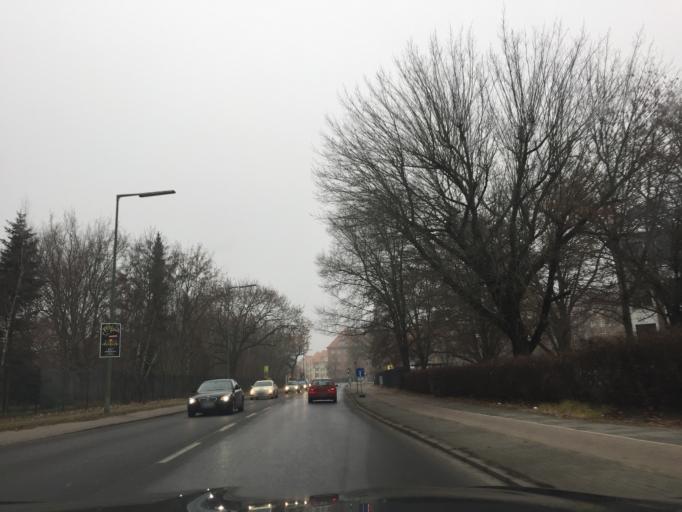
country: DE
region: Berlin
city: Siemensstadt
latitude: 52.5323
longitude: 13.2669
